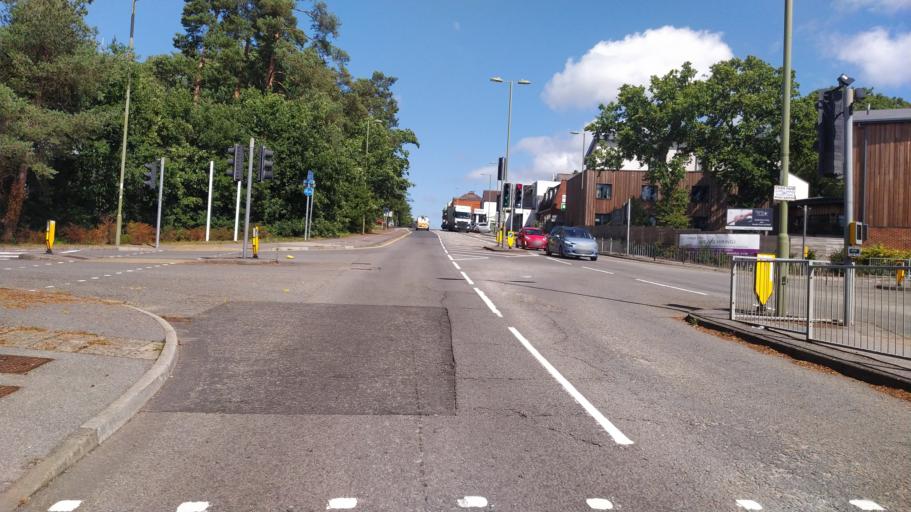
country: GB
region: England
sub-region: Hampshire
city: Bordon
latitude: 51.1099
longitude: -0.8646
